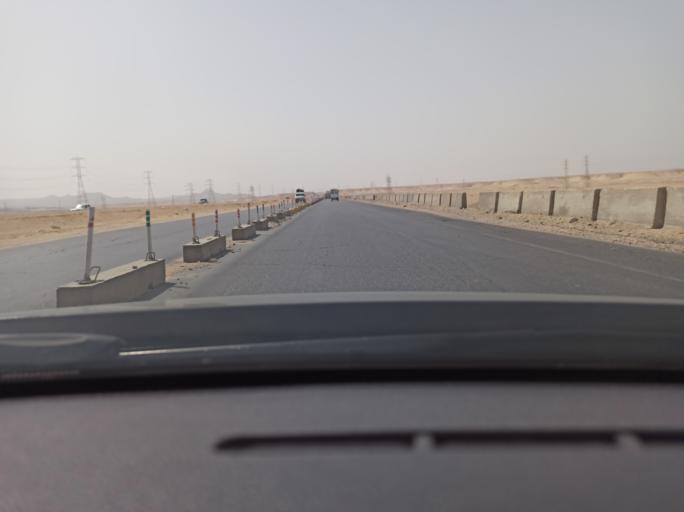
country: EG
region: Muhafazat Bani Suwayf
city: Bush
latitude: 29.1670
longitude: 31.2400
